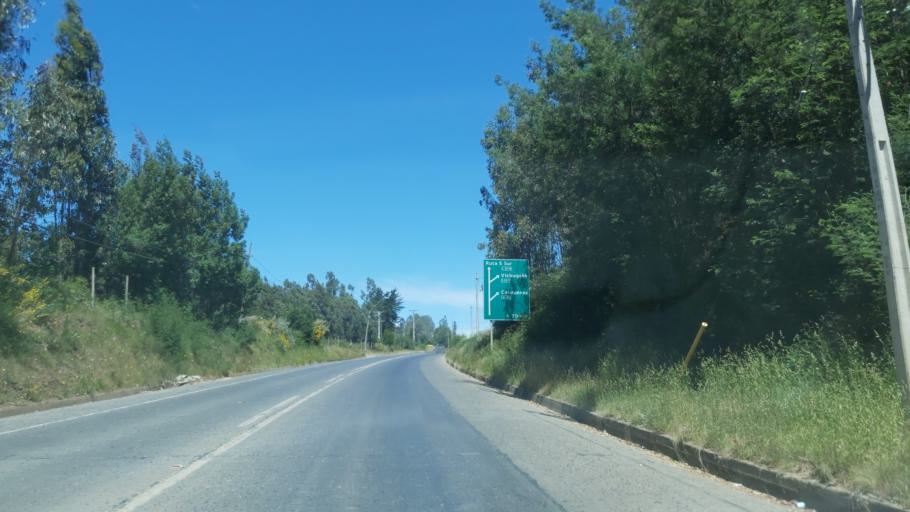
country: CL
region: Maule
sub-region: Provincia de Talca
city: Constitucion
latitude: -35.3582
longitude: -72.4068
